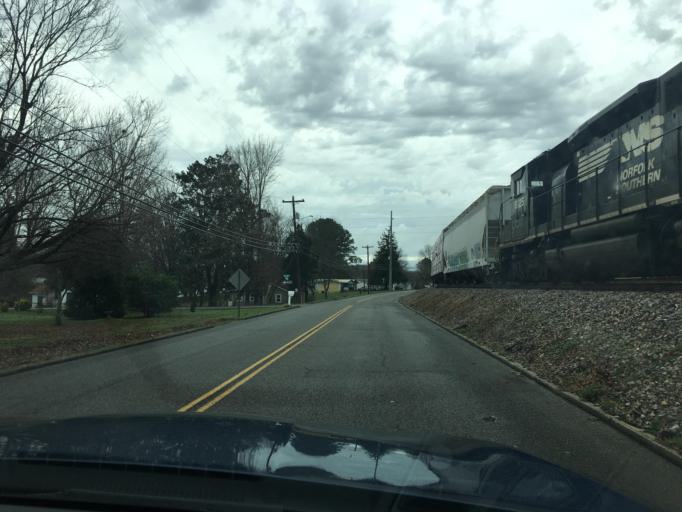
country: US
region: Tennessee
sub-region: McMinn County
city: Athens
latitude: 35.4595
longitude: -84.6061
